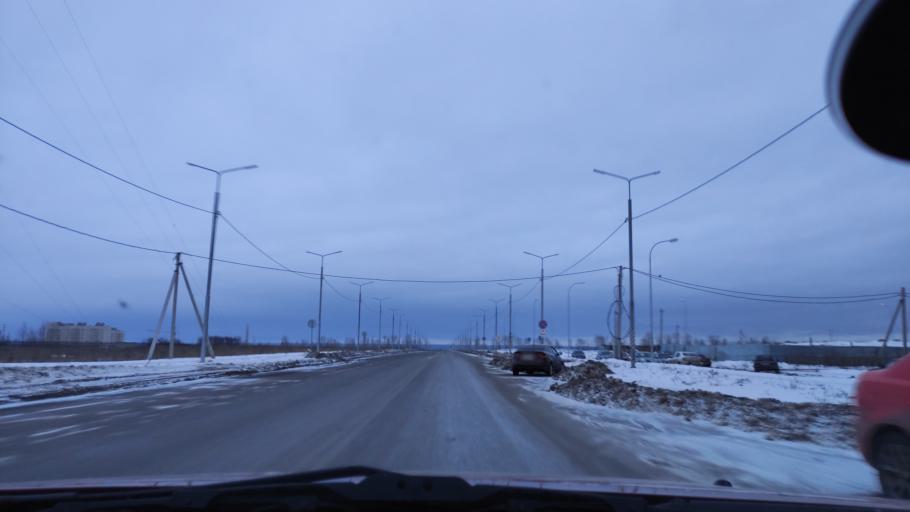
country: RU
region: Tambov
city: Tambov
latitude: 52.7773
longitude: 41.4125
